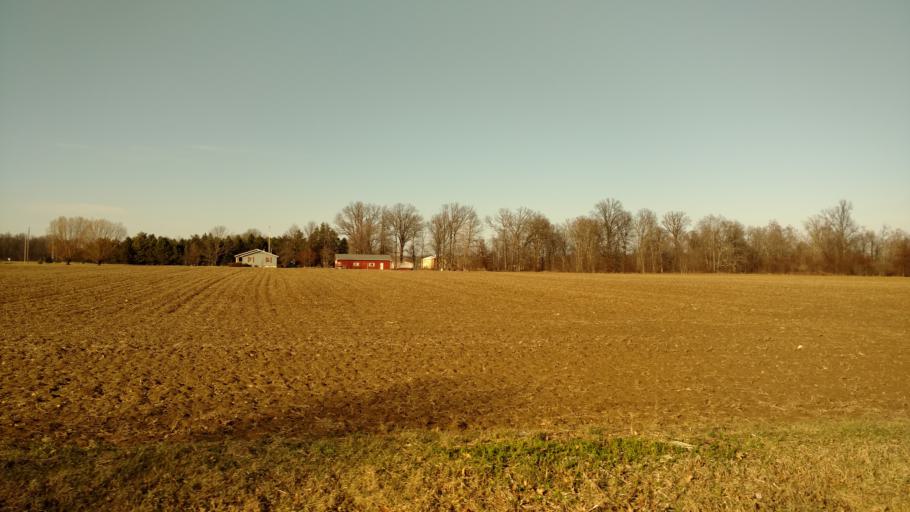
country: US
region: Ohio
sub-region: Crawford County
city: Galion
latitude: 40.7119
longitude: -82.7641
